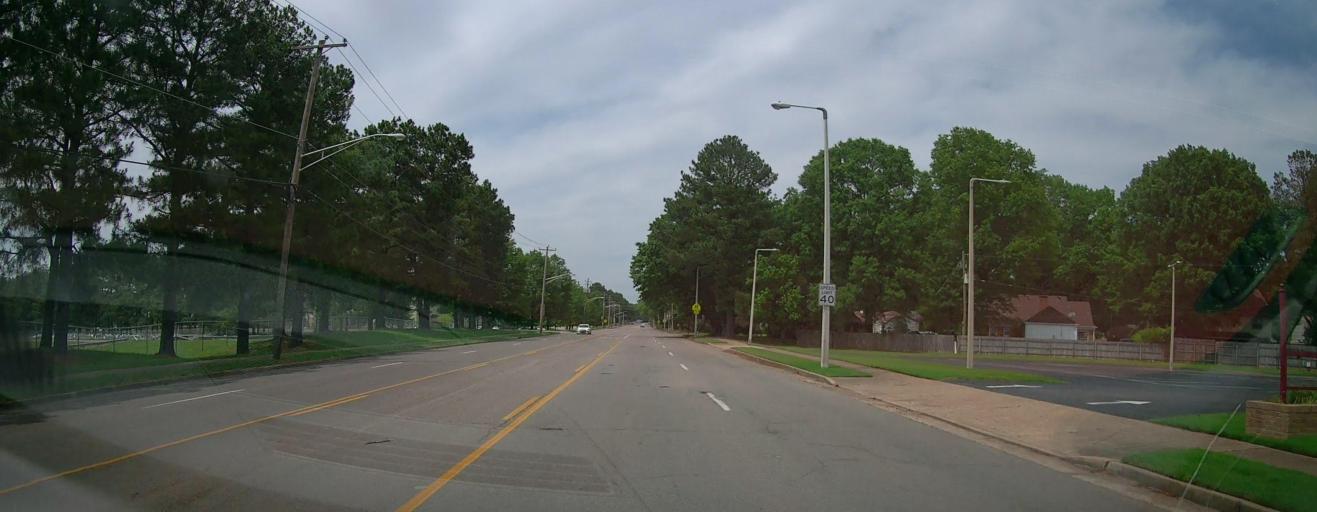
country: US
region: Tennessee
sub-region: Shelby County
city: Germantown
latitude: 35.0760
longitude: -89.8503
